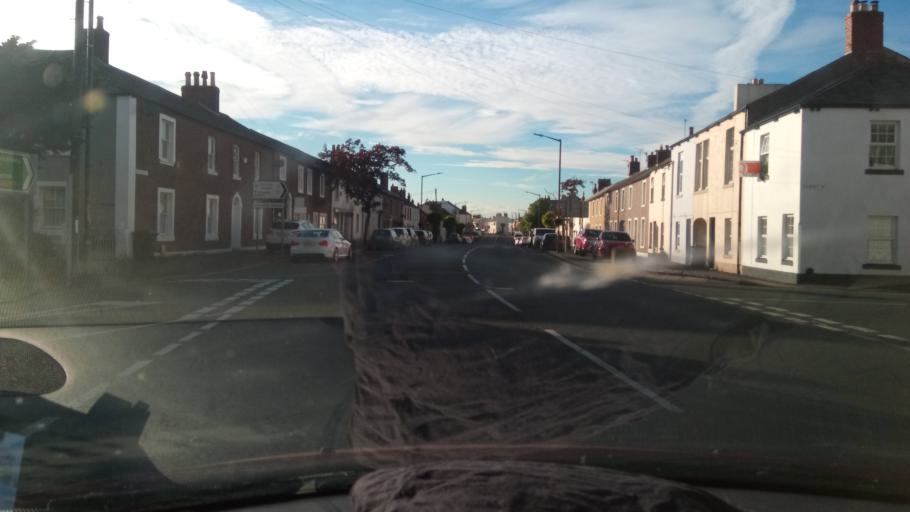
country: GB
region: Scotland
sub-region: Dumfries and Galloway
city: Gretna
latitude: 55.0068
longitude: -2.9707
